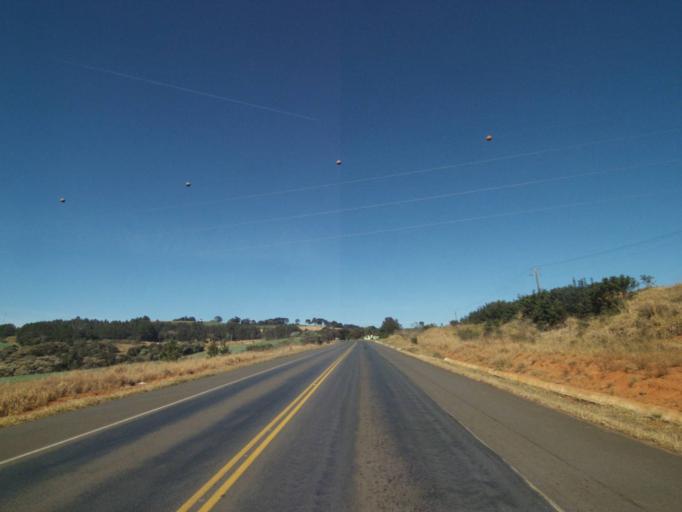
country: BR
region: Parana
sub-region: Tibagi
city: Tibagi
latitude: -24.4971
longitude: -50.4452
